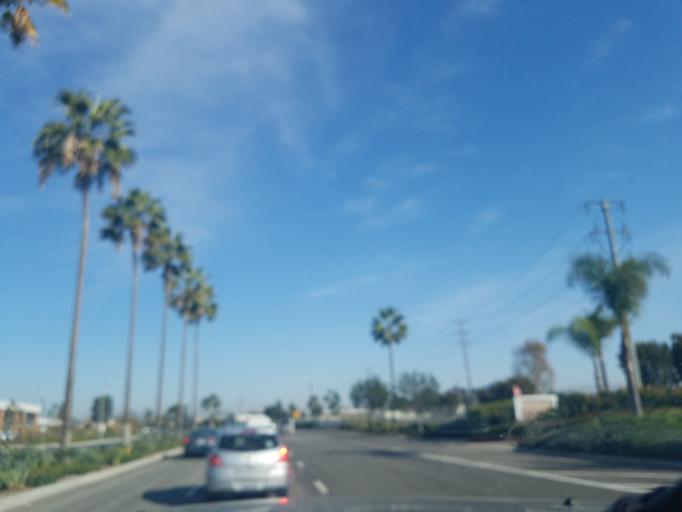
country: US
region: California
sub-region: Orange County
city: Irvine
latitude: 33.6868
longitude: -117.8545
